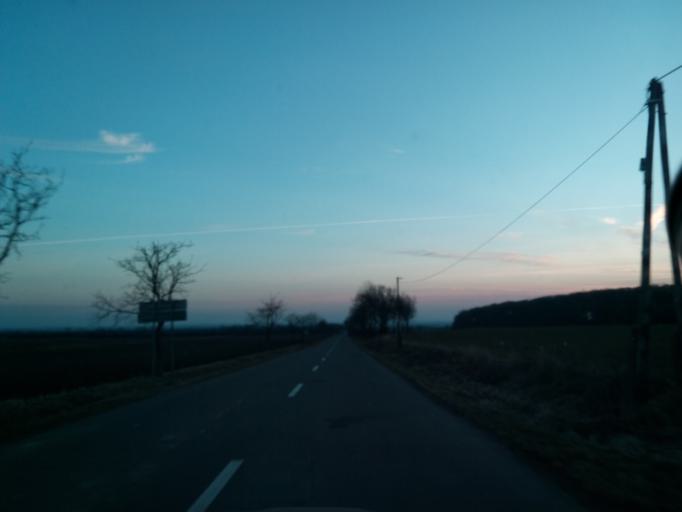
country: SK
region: Kosicky
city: Sobrance
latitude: 48.8041
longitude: 22.1552
